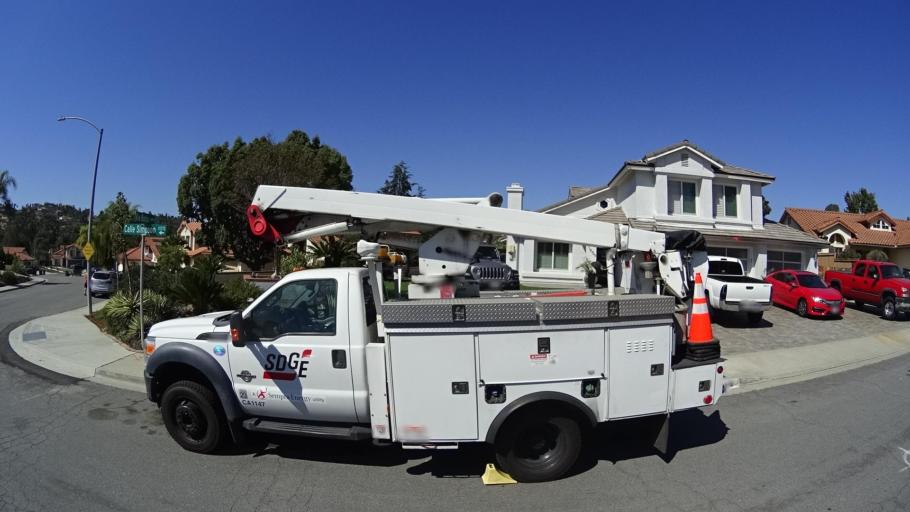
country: US
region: California
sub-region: San Diego County
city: Rancho San Diego
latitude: 32.7572
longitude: -116.9408
